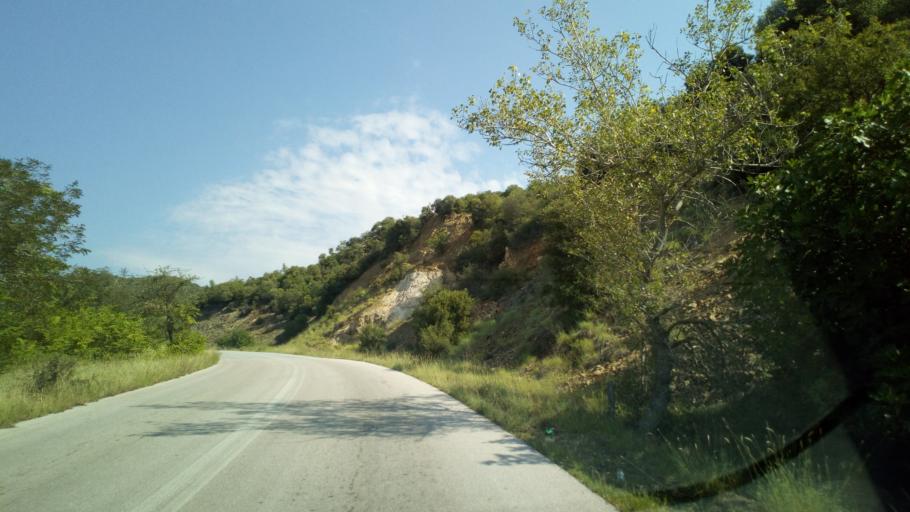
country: GR
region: Central Macedonia
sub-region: Nomos Thessalonikis
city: Askos
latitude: 40.7263
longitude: 23.3762
